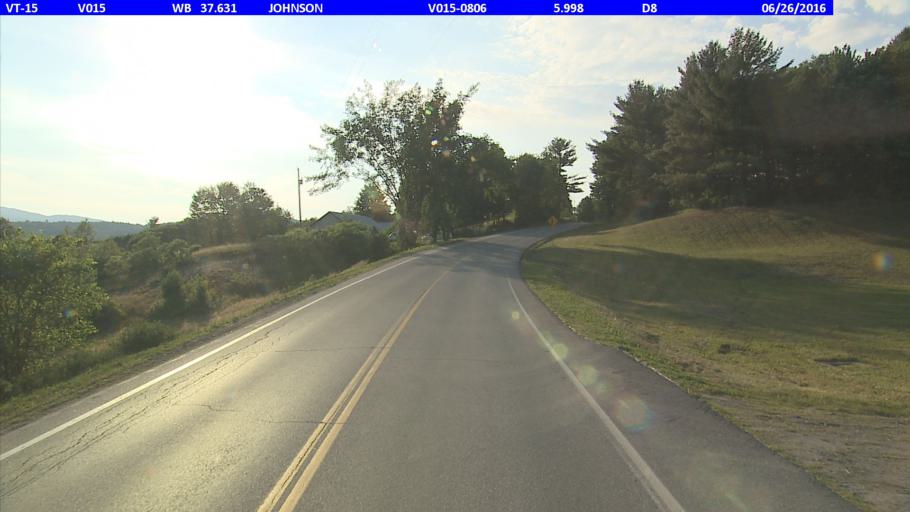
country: US
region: Vermont
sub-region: Lamoille County
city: Johnson
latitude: 44.6158
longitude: -72.6608
